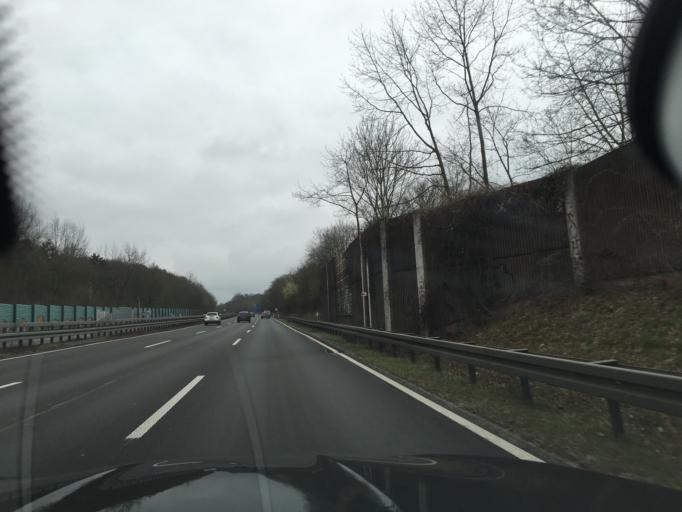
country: DE
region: North Rhine-Westphalia
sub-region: Regierungsbezirk Koln
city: Bonn
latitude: 50.7364
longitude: 7.1474
